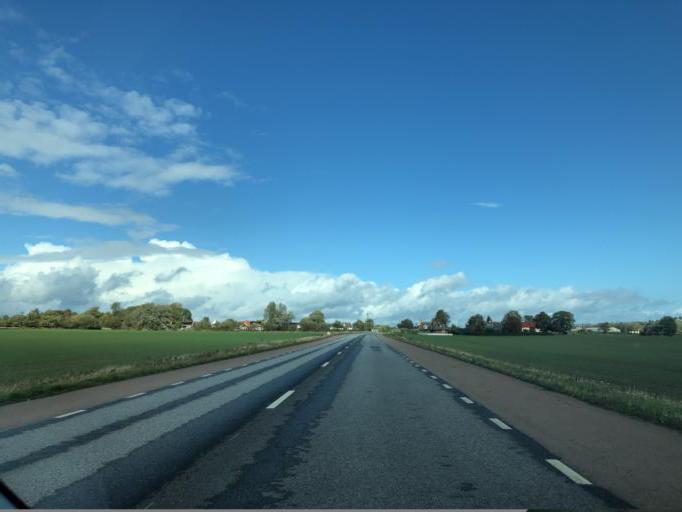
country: SE
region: Skane
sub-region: Helsingborg
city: Glumslov
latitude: 55.9141
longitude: 12.8288
